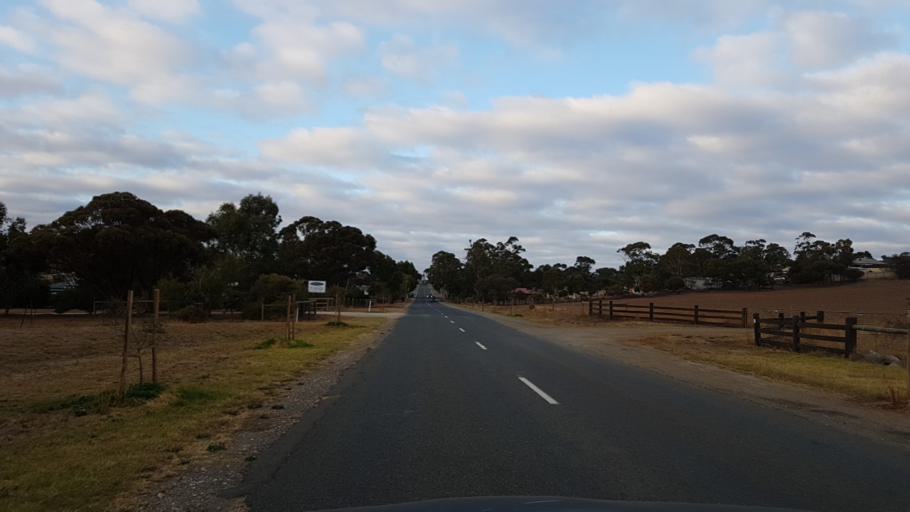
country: AU
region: South Australia
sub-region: Mount Barker
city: Callington
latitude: -35.0751
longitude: 139.0126
